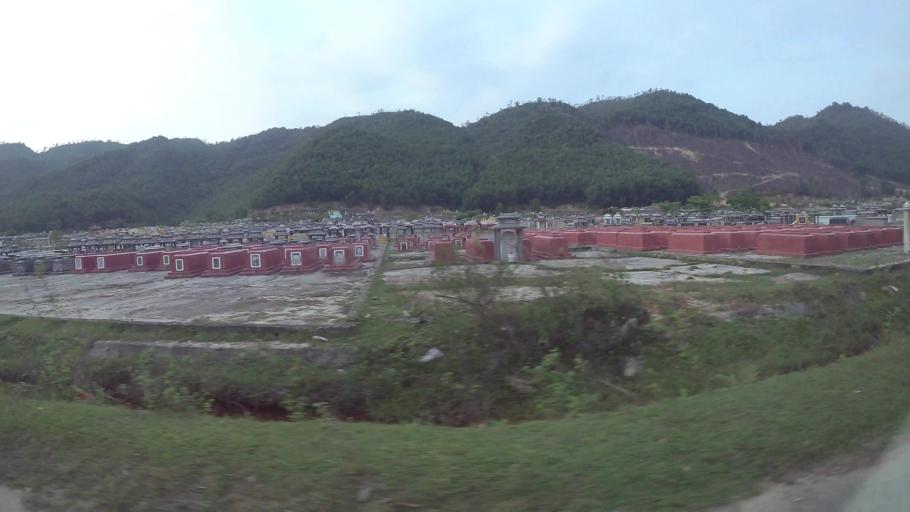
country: VN
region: Da Nang
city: Lien Chieu
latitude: 16.0595
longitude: 108.1239
